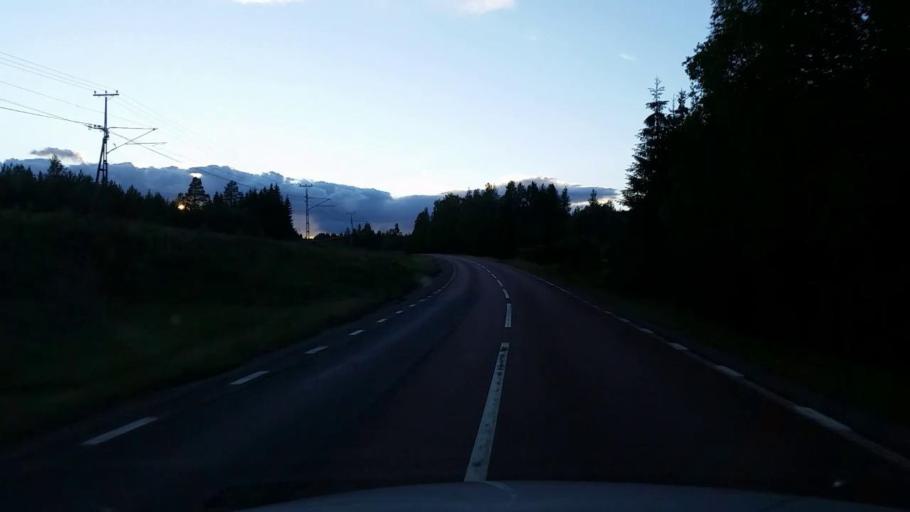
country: SE
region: Gaevleborg
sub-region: Ljusdals Kommun
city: Farila
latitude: 62.0837
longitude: 15.8145
